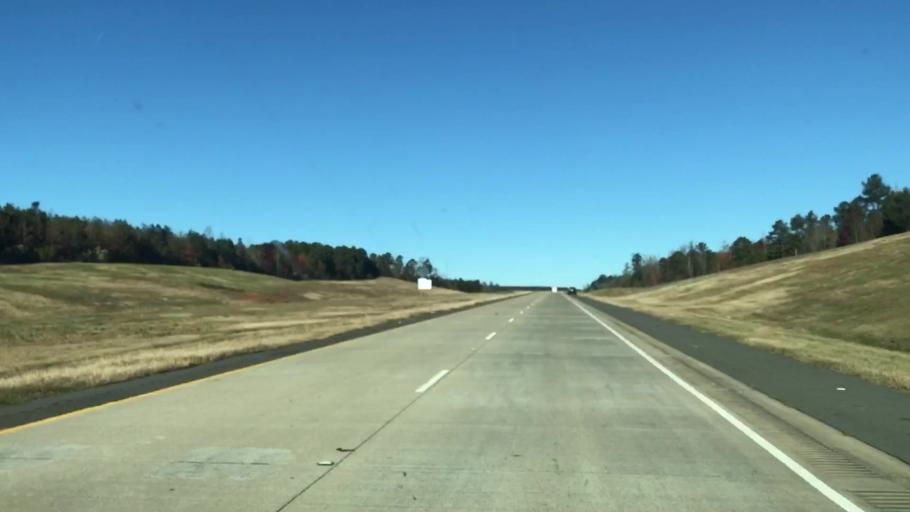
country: US
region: Louisiana
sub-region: Caddo Parish
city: Vivian
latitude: 32.9122
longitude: -93.8727
